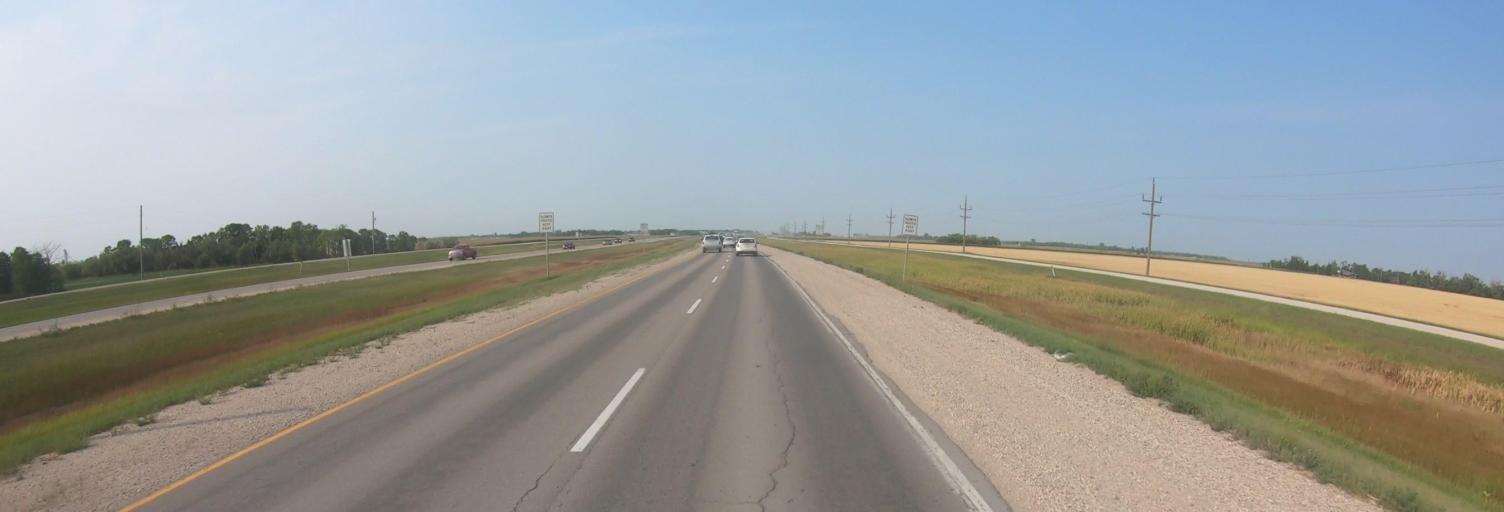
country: CA
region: Manitoba
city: Steinbach
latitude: 49.5771
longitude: -96.6867
